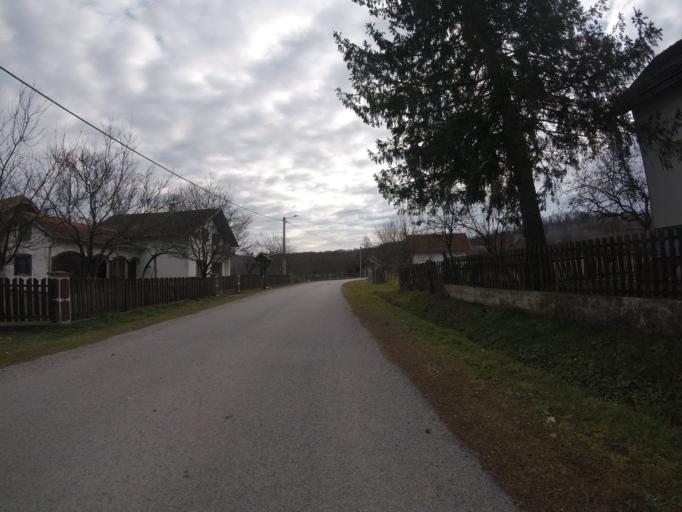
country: HR
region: Sisacko-Moslavacka
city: Glina
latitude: 45.4298
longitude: 16.0881
